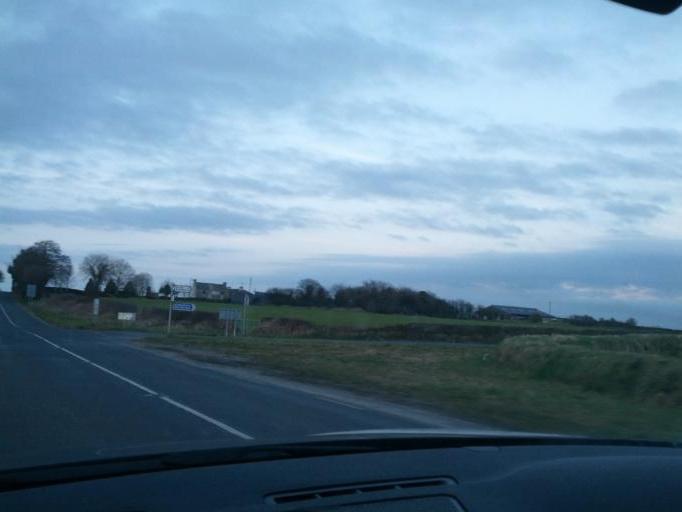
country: IE
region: Connaught
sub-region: County Galway
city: Portumna
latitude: 53.0458
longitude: -8.1097
